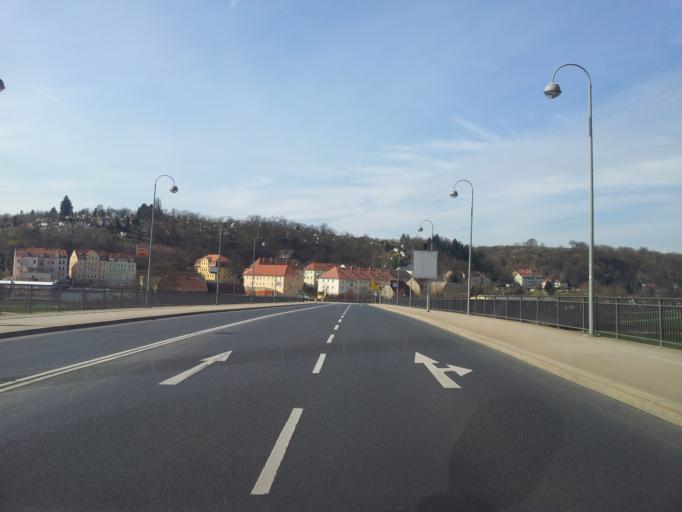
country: DE
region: Saxony
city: Meissen
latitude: 51.1706
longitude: 13.4739
